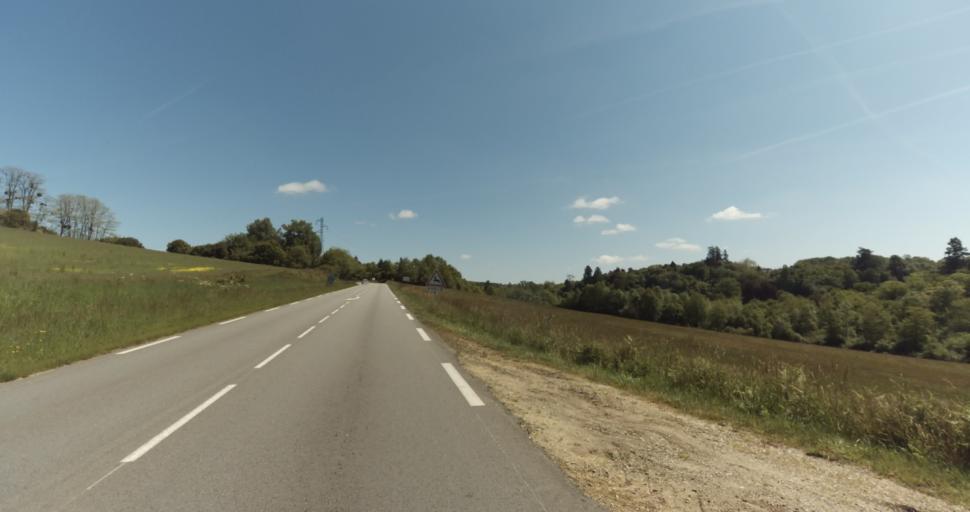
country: FR
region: Limousin
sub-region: Departement de la Haute-Vienne
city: Le Vigen
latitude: 45.7588
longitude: 1.2921
